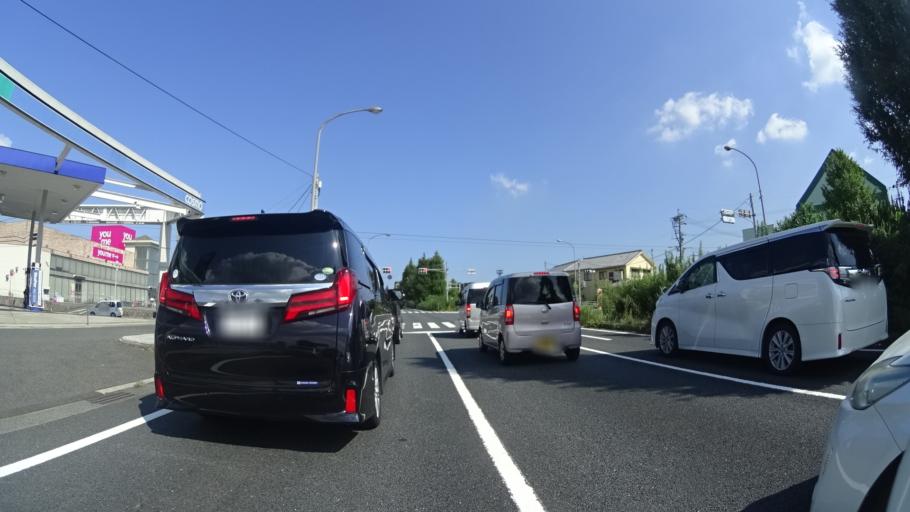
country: JP
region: Fukuoka
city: Kanda
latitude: 33.8111
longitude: 130.9461
